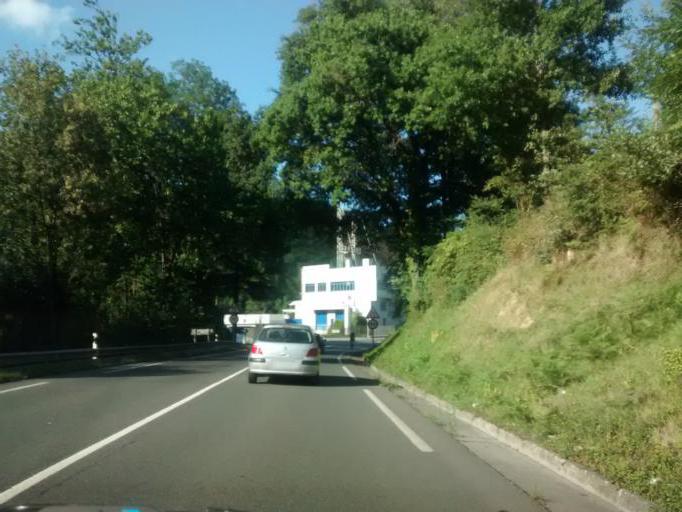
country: ES
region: Basque Country
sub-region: Provincia de Guipuzcoa
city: Elgoibar
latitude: 43.2258
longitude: -2.4076
